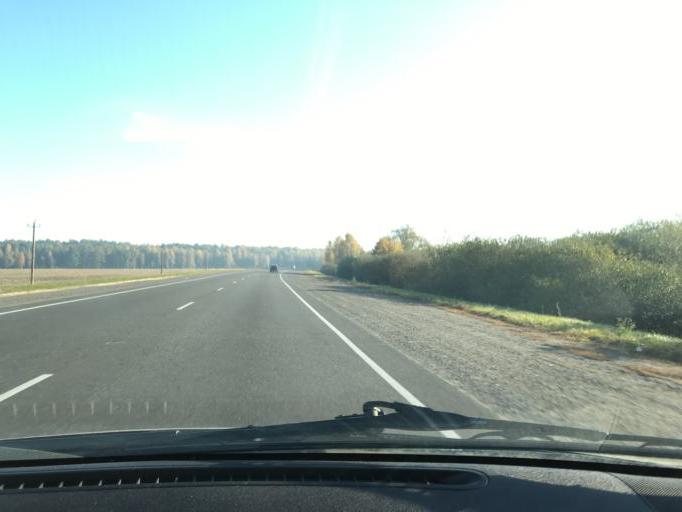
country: BY
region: Brest
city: Asnyezhytsy
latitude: 52.2264
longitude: 26.1383
